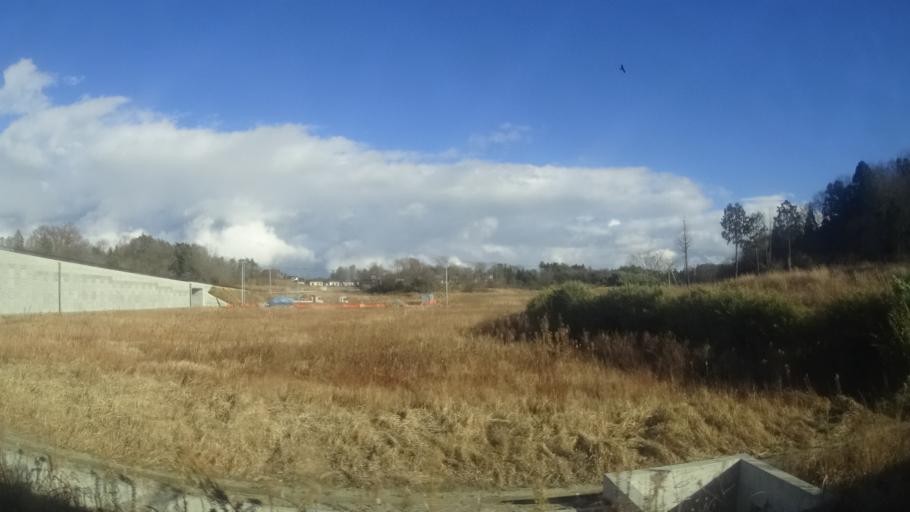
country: JP
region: Miyagi
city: Marumori
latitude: 37.8658
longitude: 140.9288
